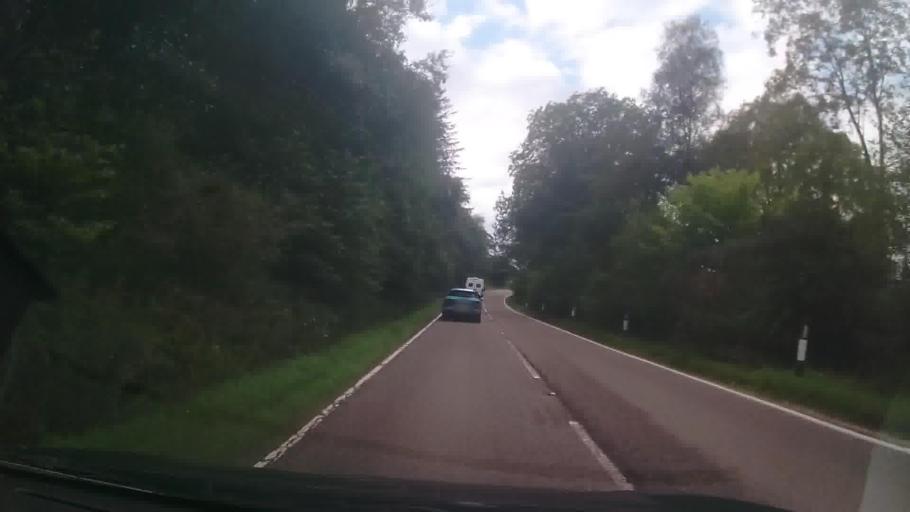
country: GB
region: Scotland
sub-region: Highland
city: Fort William
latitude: 56.6860
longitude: -5.2150
